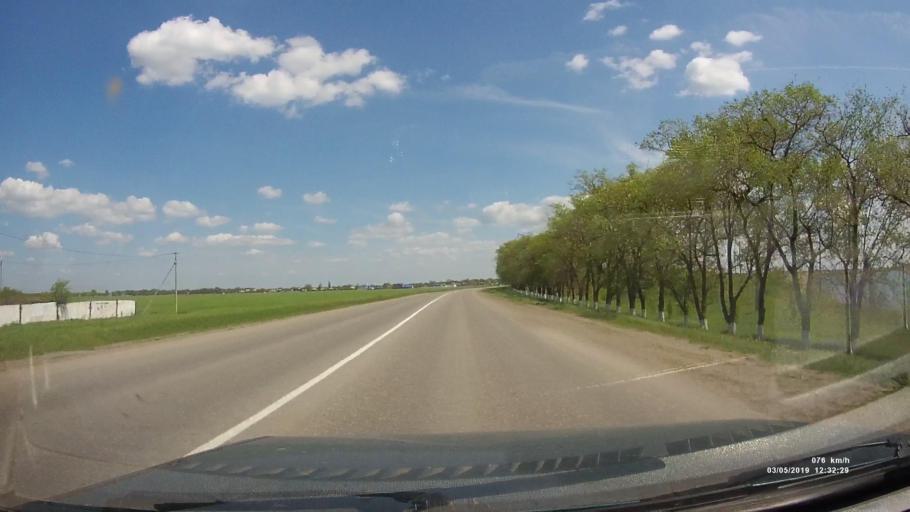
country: RU
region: Rostov
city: Semikarakorsk
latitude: 47.5119
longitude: 40.7603
